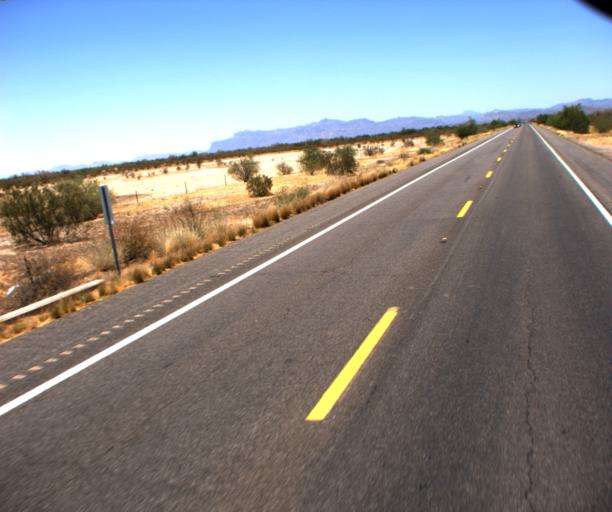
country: US
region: Arizona
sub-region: Pinal County
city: Gold Camp
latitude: 33.1856
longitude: -111.3511
